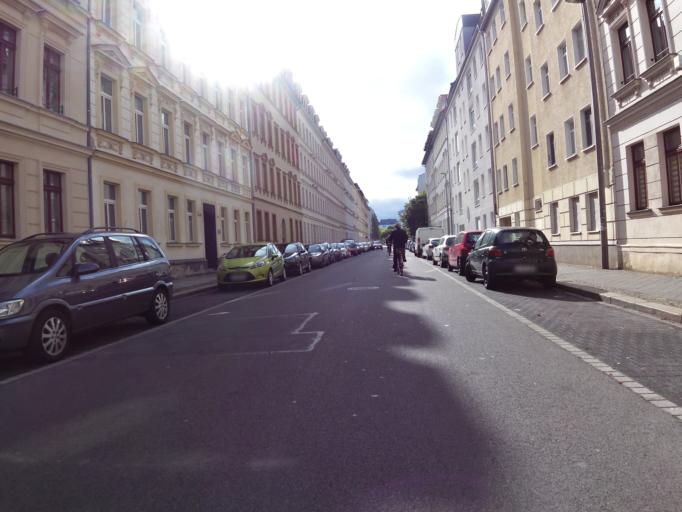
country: DE
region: Saxony
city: Leipzig
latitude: 51.3320
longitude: 12.3987
